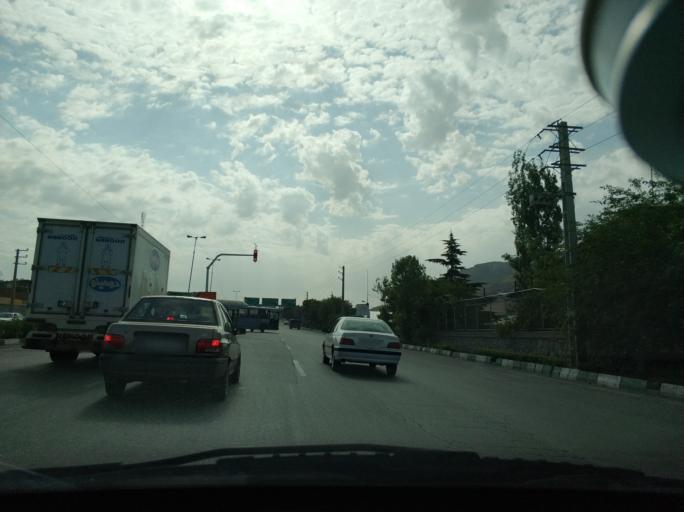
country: IR
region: Tehran
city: Tehran
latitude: 35.7238
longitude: 51.5765
